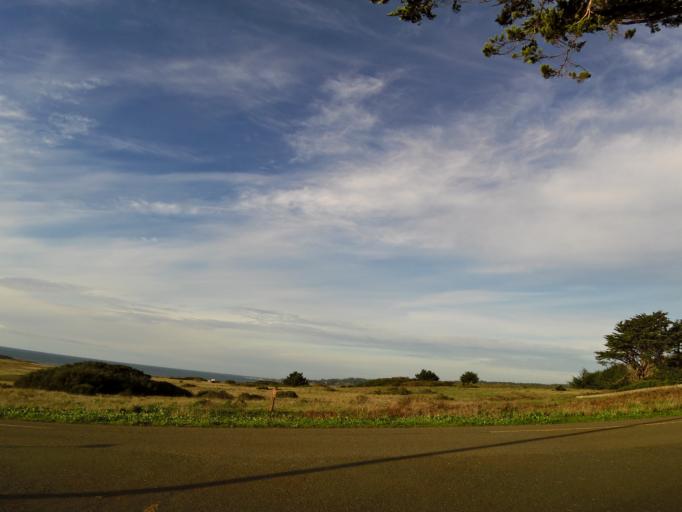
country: US
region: California
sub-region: Mendocino County
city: Fort Bragg
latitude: 39.3064
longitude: -123.8050
